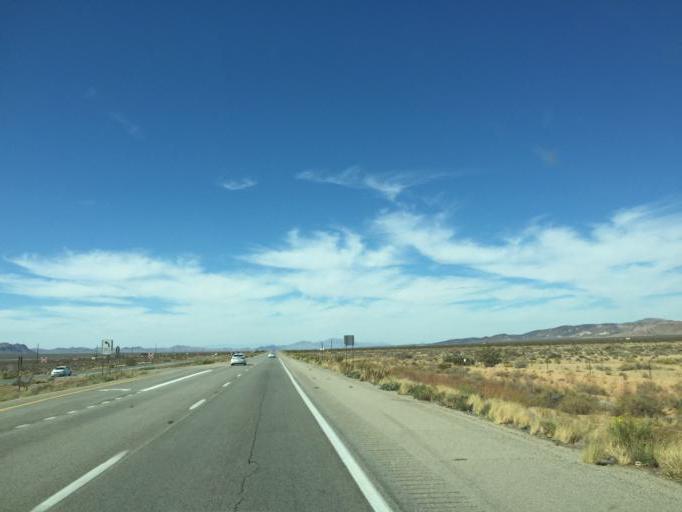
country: US
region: Arizona
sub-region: Mohave County
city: Dolan Springs
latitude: 35.5603
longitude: -114.3734
